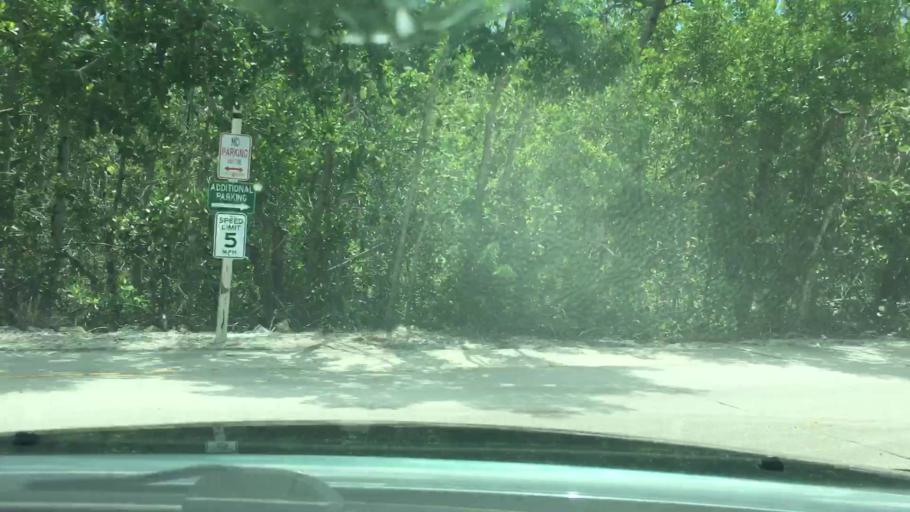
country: US
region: Florida
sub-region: Collier County
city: Marco
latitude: 25.9489
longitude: -81.7428
